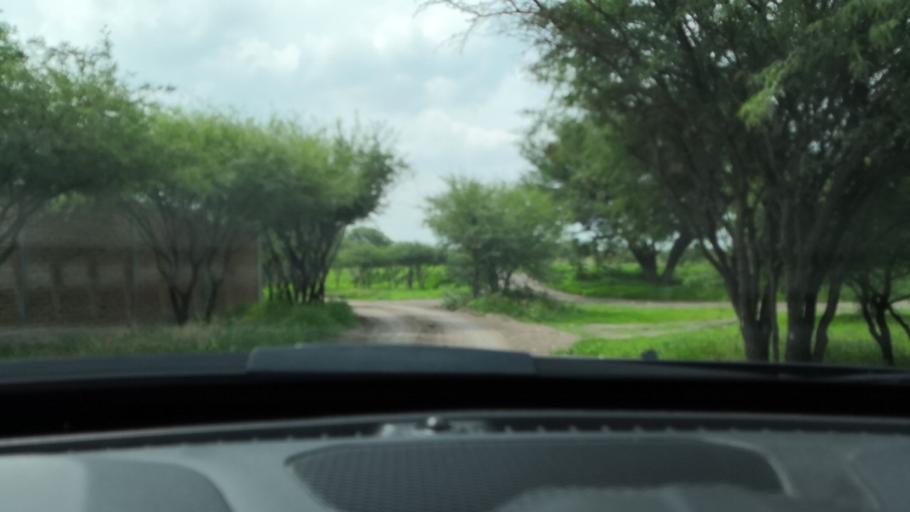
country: MX
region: Guanajuato
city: Leon
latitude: 21.1921
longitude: -101.6839
